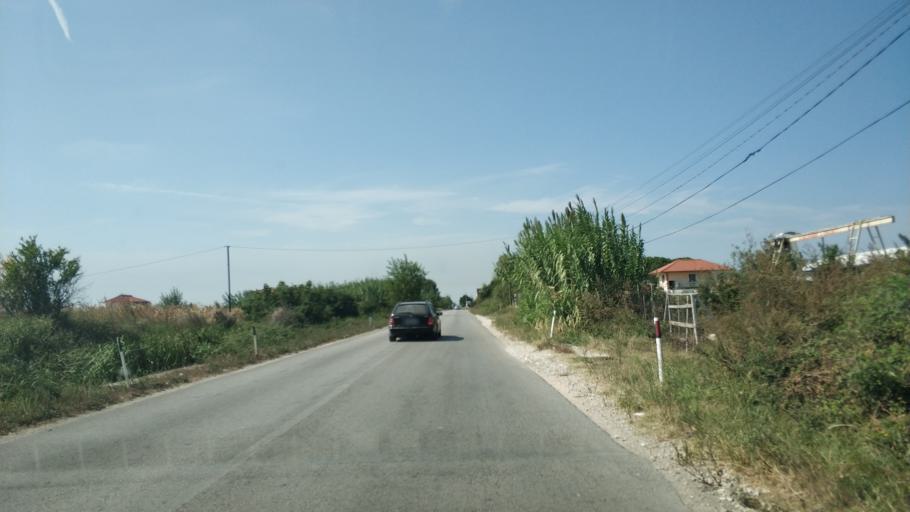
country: AL
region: Fier
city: Fier
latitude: 40.7345
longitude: 19.5280
